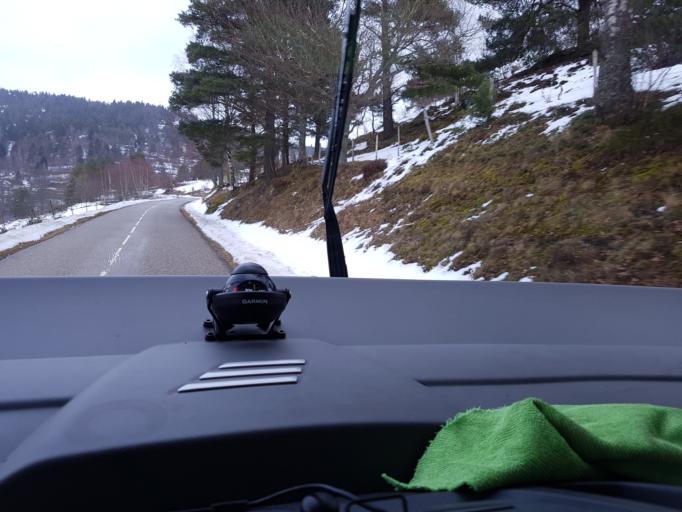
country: FR
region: Alsace
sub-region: Departement du Haut-Rhin
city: Soultzeren
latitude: 48.0780
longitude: 7.1048
